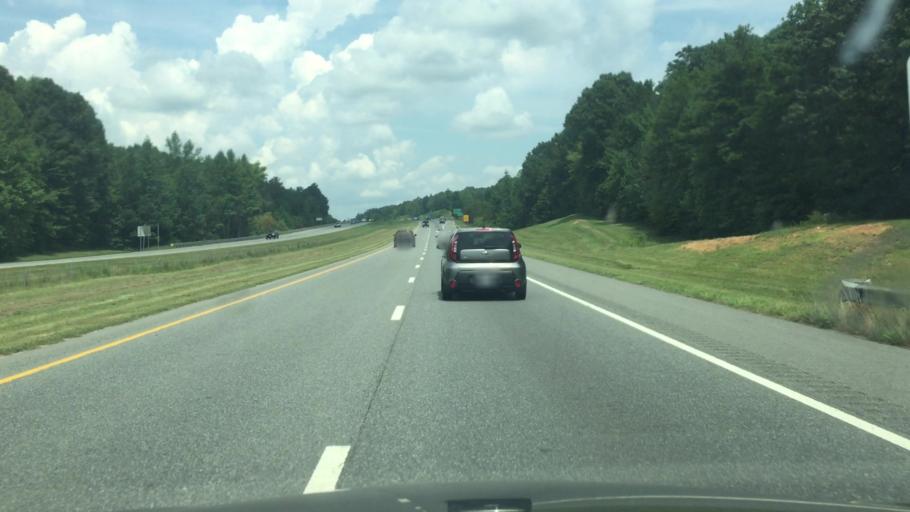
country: US
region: North Carolina
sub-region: Montgomery County
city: Biscoe
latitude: 35.5084
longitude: -79.7811
